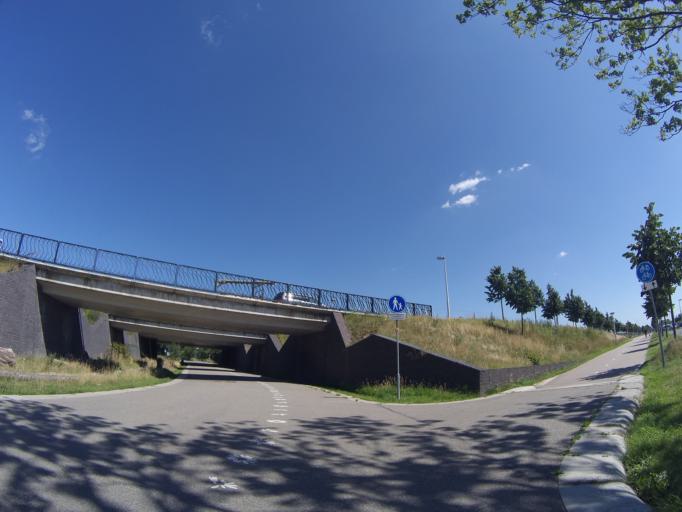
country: NL
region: Utrecht
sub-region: Stichtse Vecht
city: Maarssen
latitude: 52.1007
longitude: 5.0303
